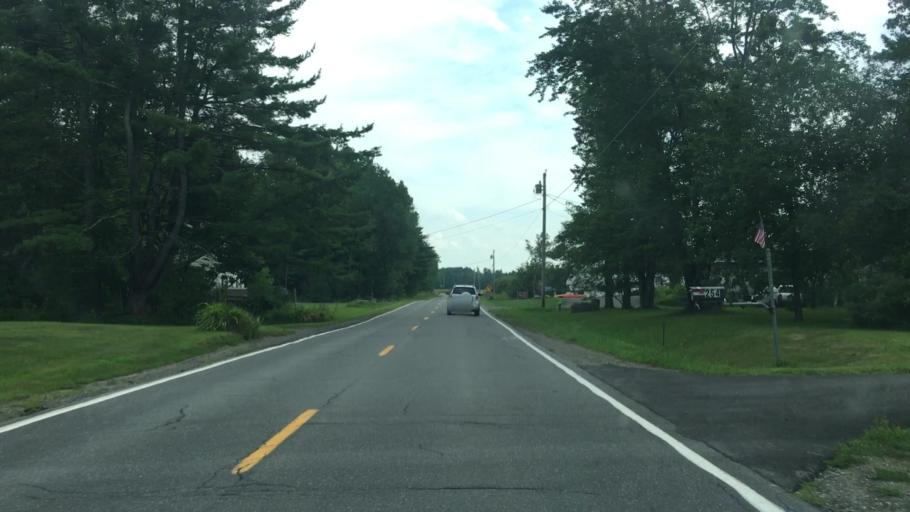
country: US
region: Maine
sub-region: Kennebec County
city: Vassalboro
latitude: 44.4419
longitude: -69.6057
